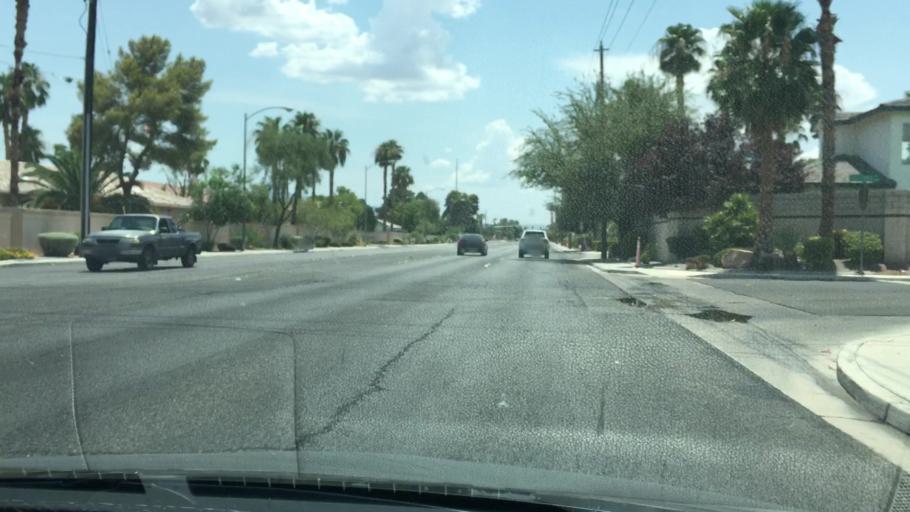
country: US
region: Nevada
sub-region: Clark County
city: Whitney
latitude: 36.0823
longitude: -115.0916
